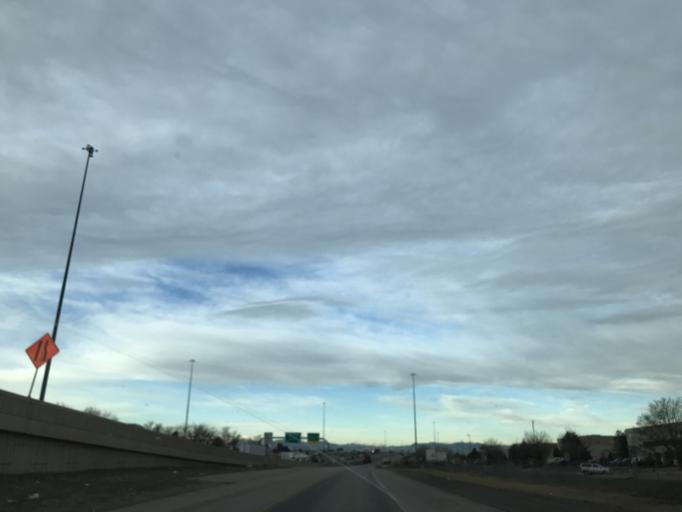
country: US
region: Colorado
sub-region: Adams County
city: Aurora
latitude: 39.7737
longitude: -104.8337
